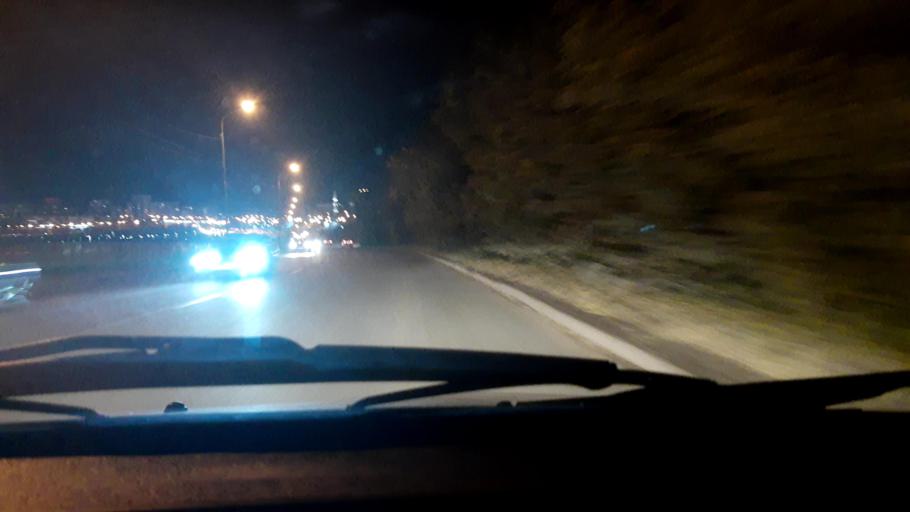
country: RU
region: Bashkortostan
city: Ufa
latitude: 54.7050
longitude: 55.9674
